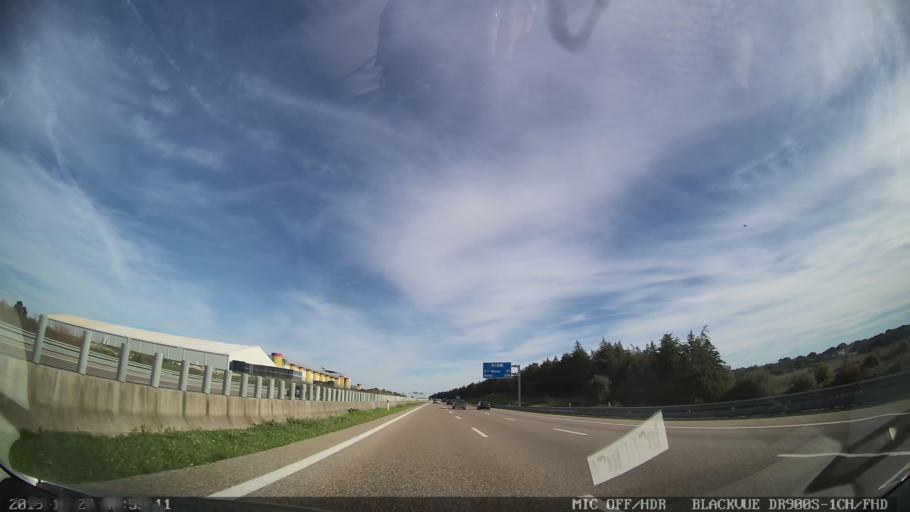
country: PT
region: Santarem
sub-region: Santarem
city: Santarem
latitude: 39.2723
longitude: -8.7147
